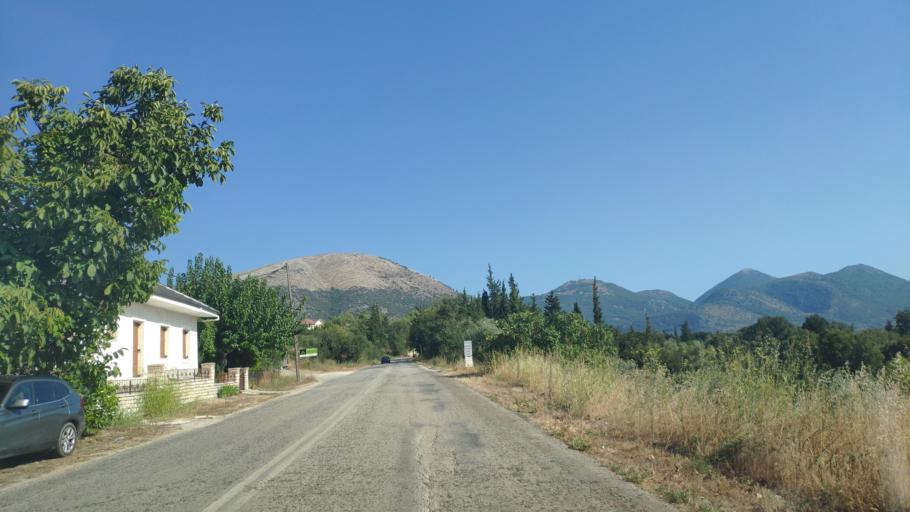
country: GR
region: Epirus
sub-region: Nomos Prevezis
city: Kanalaki
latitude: 39.2662
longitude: 20.6020
